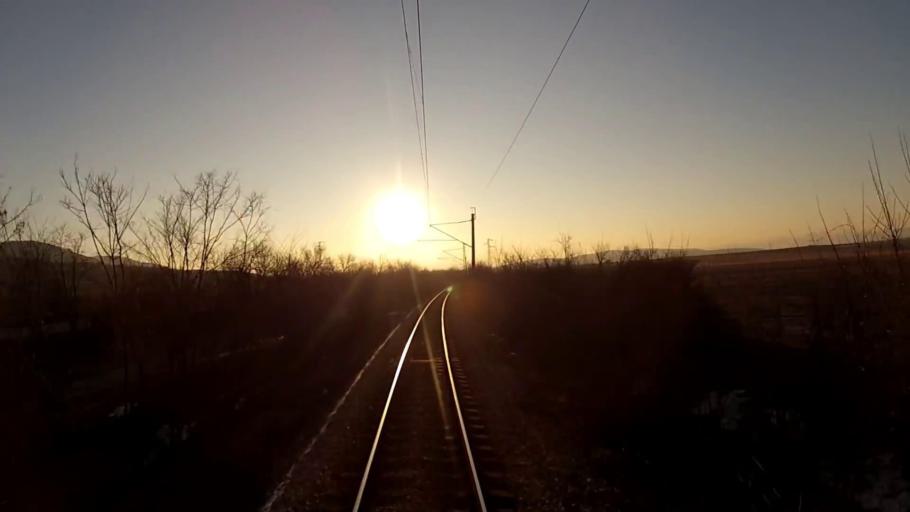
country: BG
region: Sofiya
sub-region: Obshtina Dragoman
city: Dragoman
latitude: 42.8938
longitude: 22.9705
